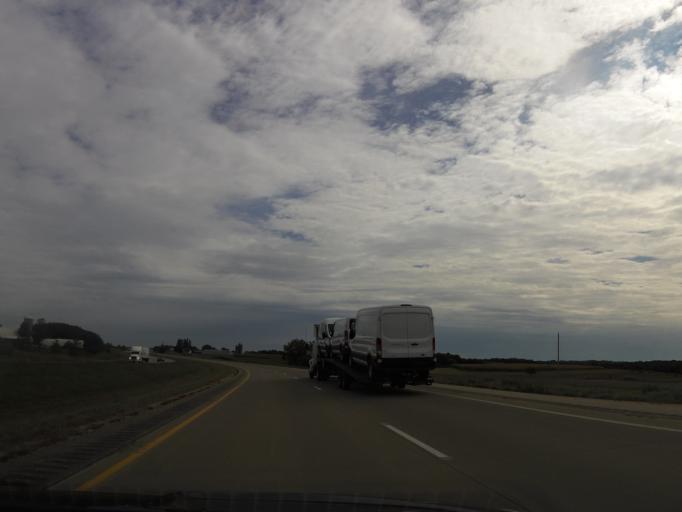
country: US
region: Wisconsin
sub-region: Trempealeau County
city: Trempealeau
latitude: 43.9119
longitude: -91.5194
